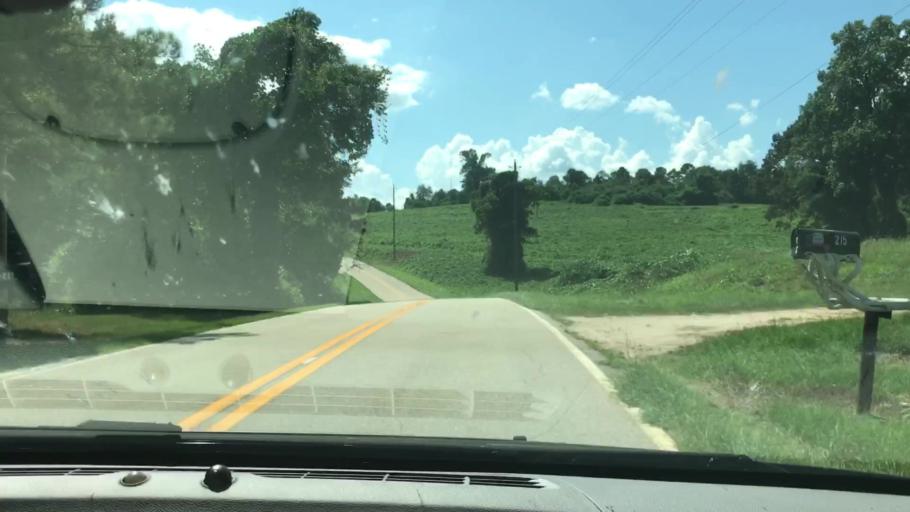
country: US
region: Georgia
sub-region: Troup County
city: La Grange
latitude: 33.1302
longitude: -85.1254
